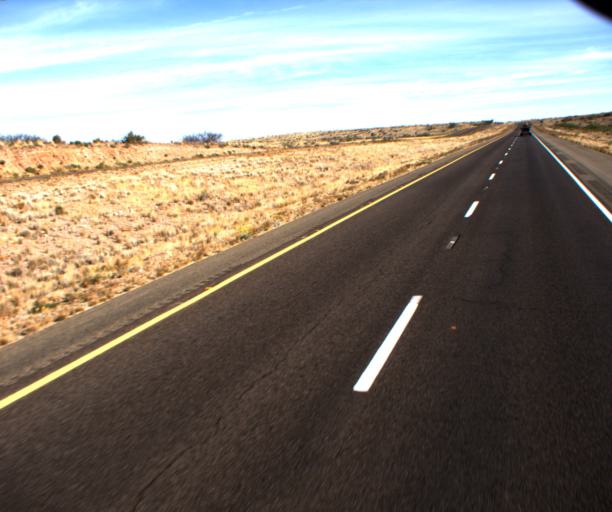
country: US
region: Arizona
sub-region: Cochise County
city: Willcox
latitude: 32.3870
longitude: -109.6658
